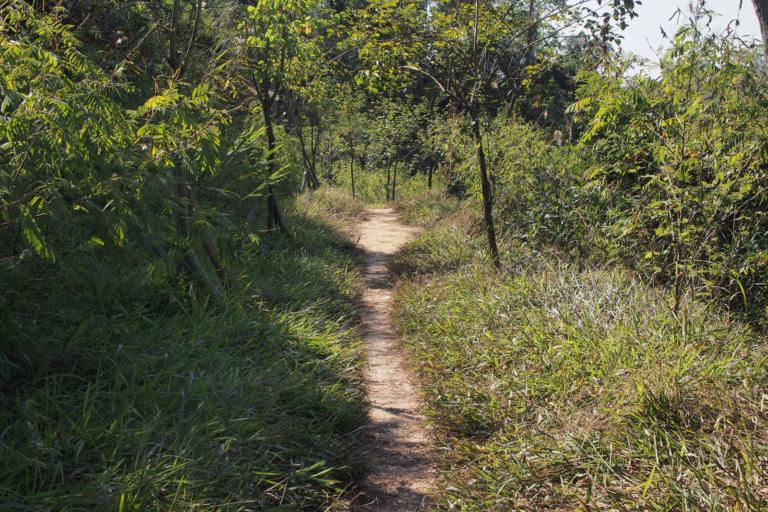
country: CN
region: Guangdong
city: Huancheng
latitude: 22.4649
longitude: 113.4146
